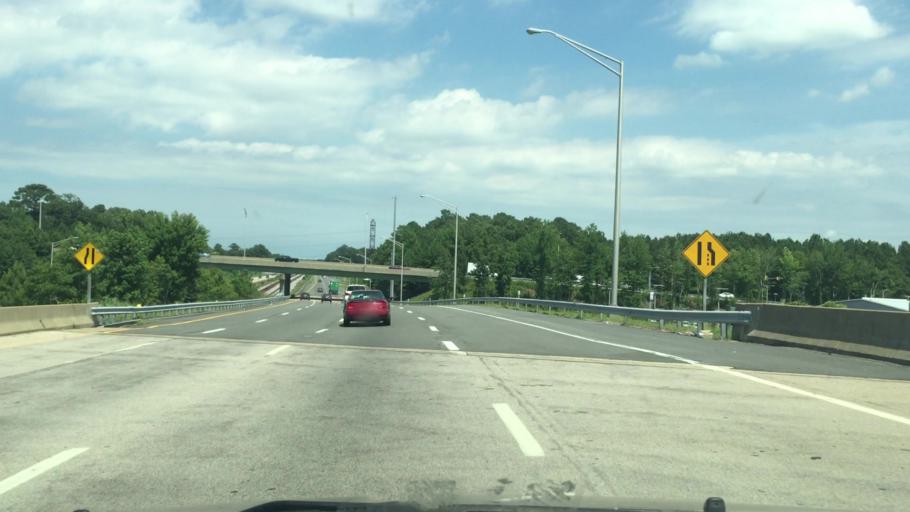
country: US
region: Virginia
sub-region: City of Portsmouth
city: Portsmouth Heights
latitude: 36.8670
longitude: -76.4246
